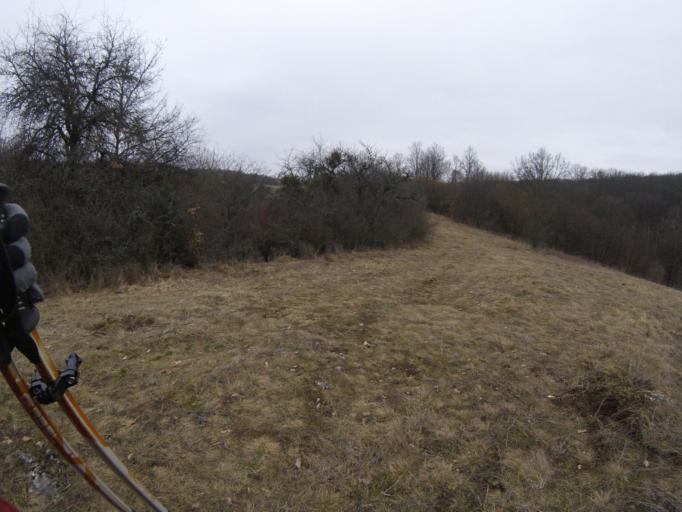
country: HU
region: Borsod-Abauj-Zemplen
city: Rudabanya
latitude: 48.4580
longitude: 20.6074
